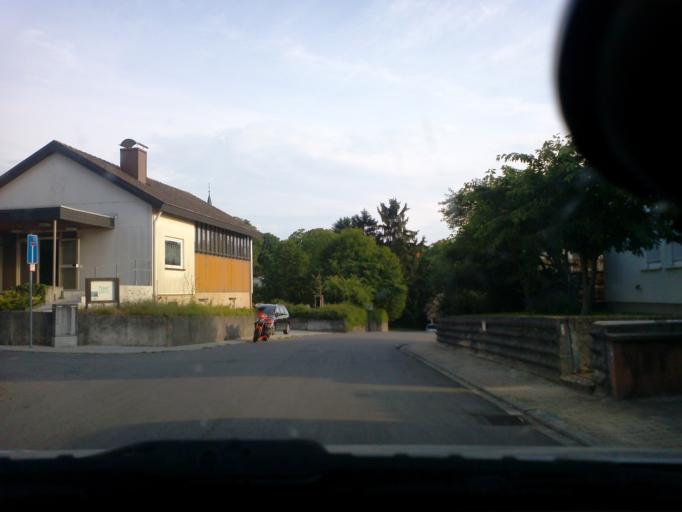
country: DE
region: Baden-Wuerttemberg
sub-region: Karlsruhe Region
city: Bretten
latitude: 48.9910
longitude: 8.6929
